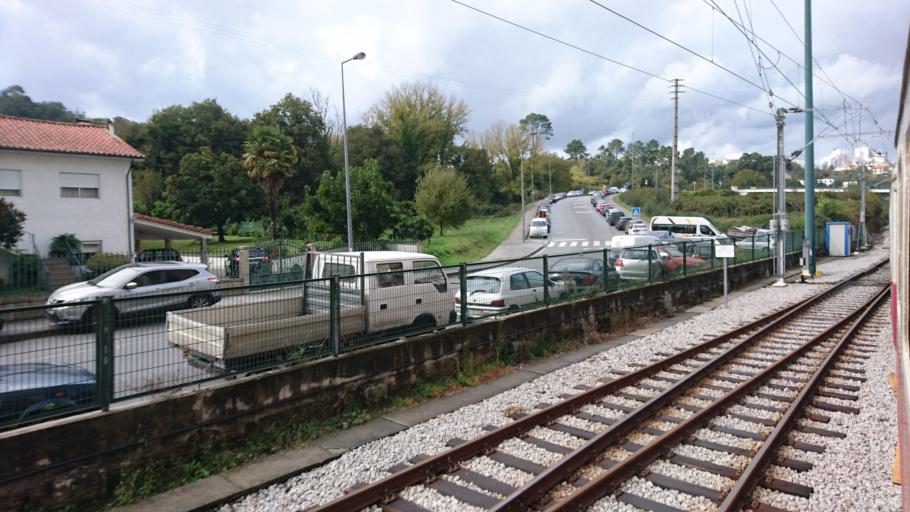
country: PT
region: Porto
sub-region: Marco de Canaveses
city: Marco de Canavezes
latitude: 41.1821
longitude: -8.1378
